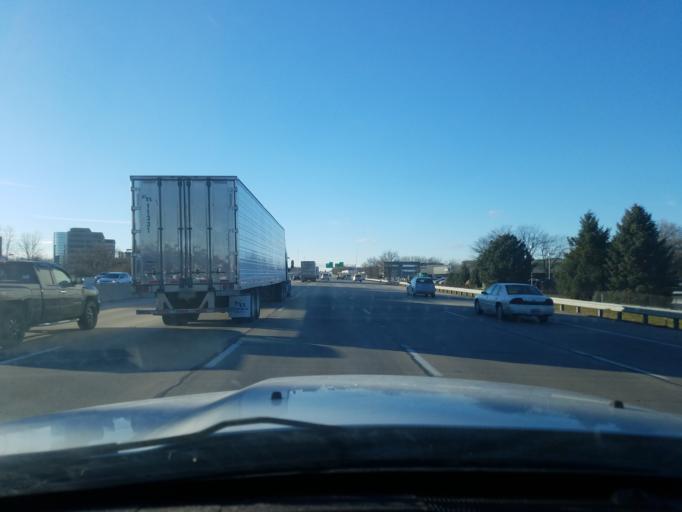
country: US
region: Indiana
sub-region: Hamilton County
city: Carmel
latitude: 39.9187
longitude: -86.1024
